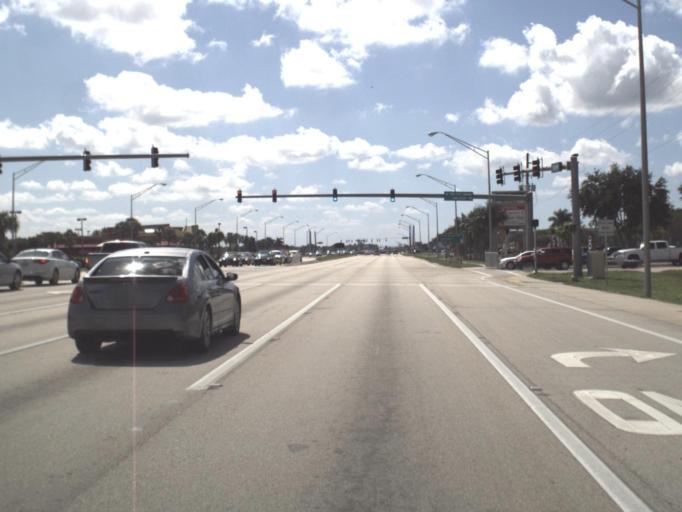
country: US
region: Florida
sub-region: Lee County
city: Pine Manor
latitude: 26.5870
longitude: -81.8720
